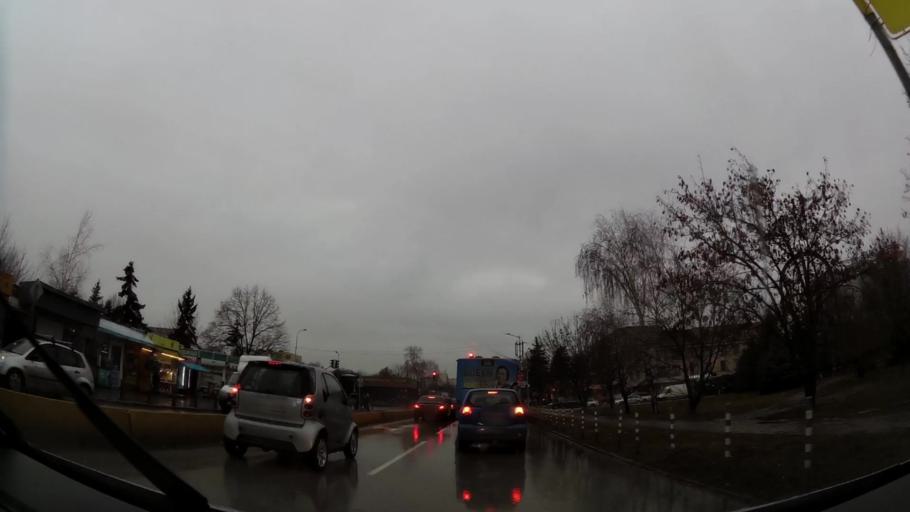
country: BG
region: Sofia-Capital
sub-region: Stolichna Obshtina
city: Sofia
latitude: 42.6520
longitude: 23.3481
